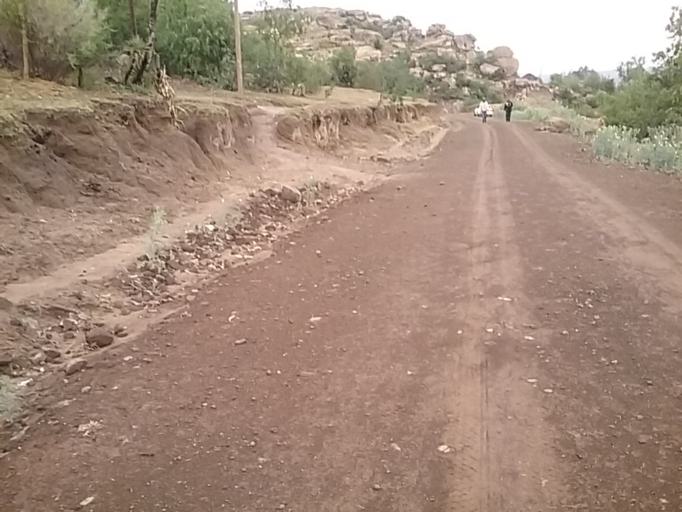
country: LS
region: Berea
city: Teyateyaneng
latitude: -29.1371
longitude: 27.7398
